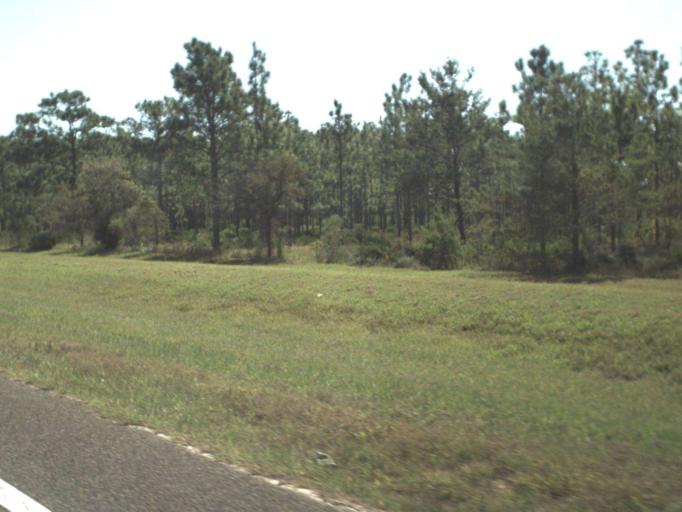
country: US
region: Florida
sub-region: Walton County
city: Seaside
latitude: 30.3636
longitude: -86.1732
